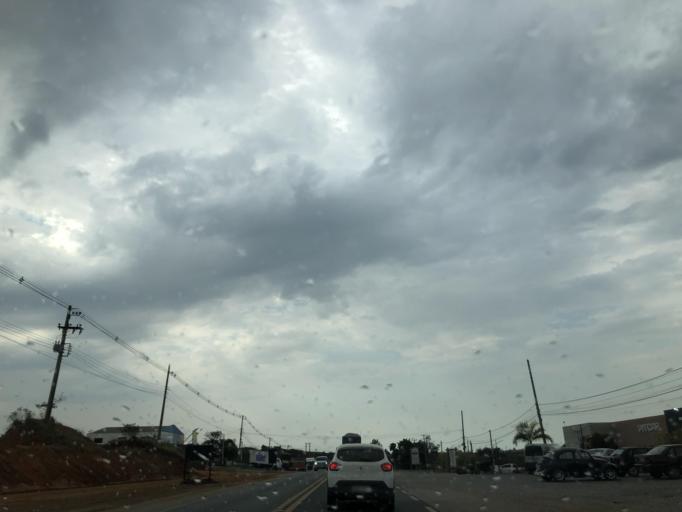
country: BR
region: Sao Paulo
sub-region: Salto De Pirapora
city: Salto de Pirapora
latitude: -23.6455
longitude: -47.5832
